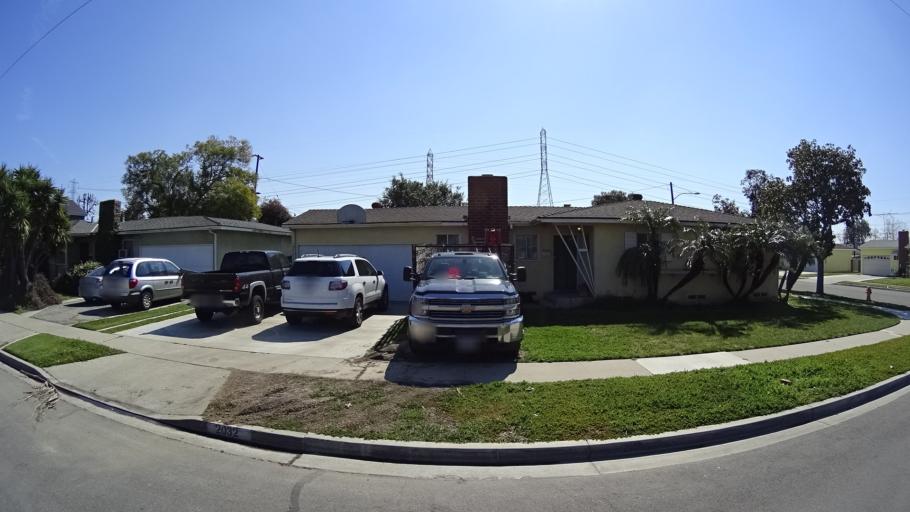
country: US
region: California
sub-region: Orange County
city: Garden Grove
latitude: 33.8084
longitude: -117.9538
